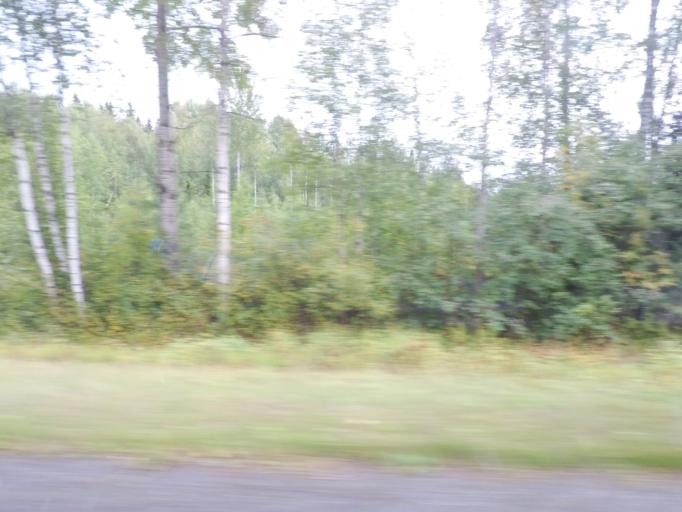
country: FI
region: Southern Savonia
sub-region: Pieksaemaeki
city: Joroinen
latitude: 62.1372
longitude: 27.8383
